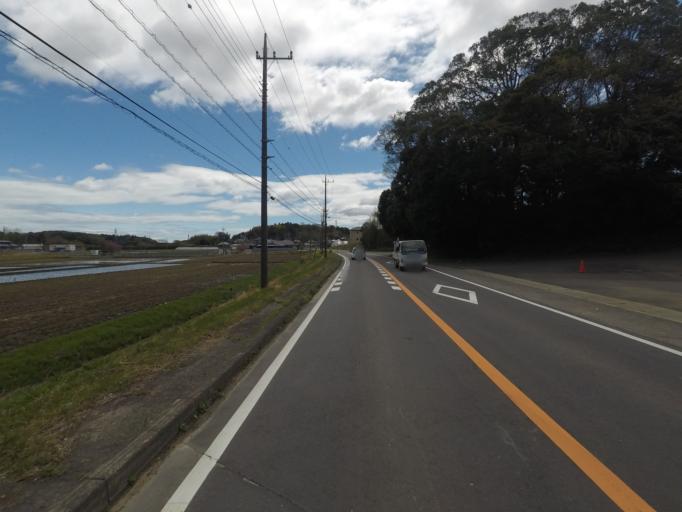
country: JP
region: Ibaraki
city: Itako
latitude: 36.1029
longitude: 140.4835
